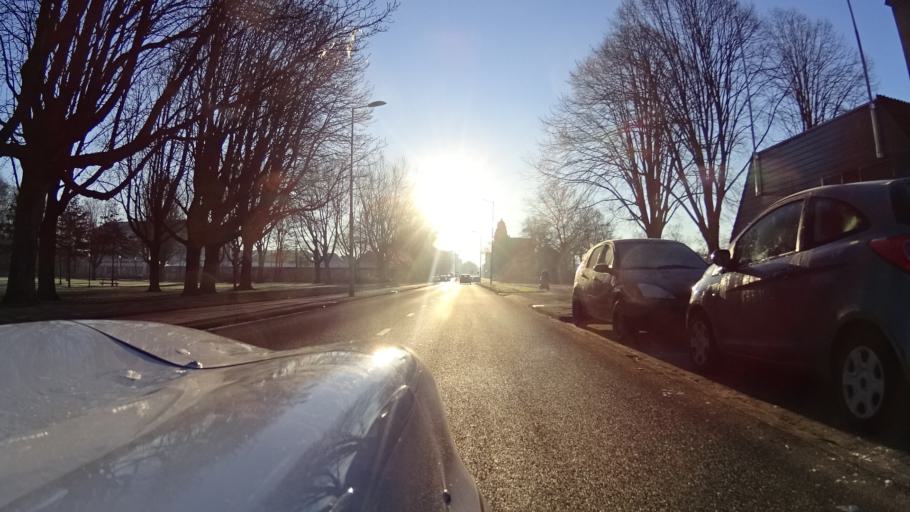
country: NL
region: South Holland
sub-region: Gemeente Rotterdam
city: Rotterdam
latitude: 51.8859
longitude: 4.4994
